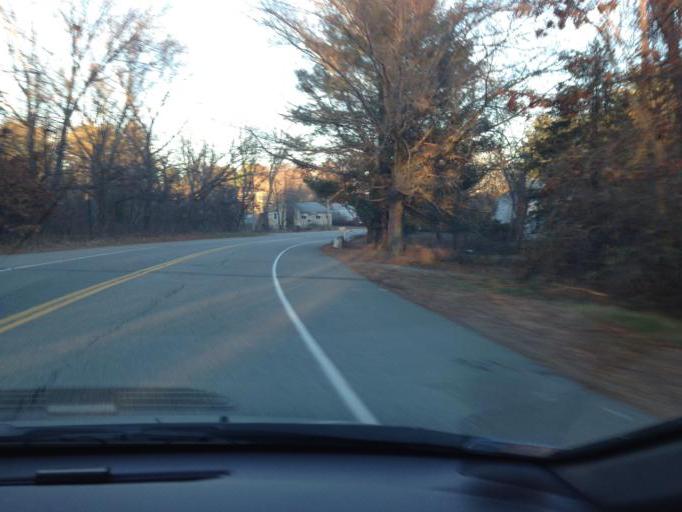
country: US
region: Massachusetts
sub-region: Middlesex County
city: Concord
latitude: 42.4800
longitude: -71.3146
